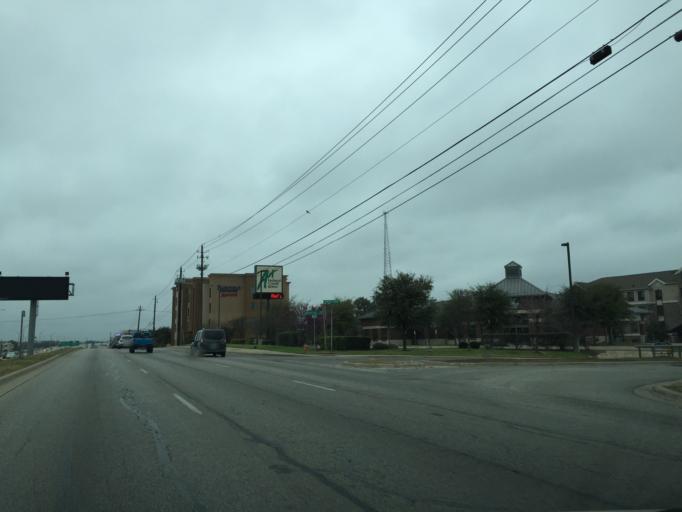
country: US
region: Texas
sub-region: Williamson County
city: Jollyville
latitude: 30.4396
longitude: -97.7788
